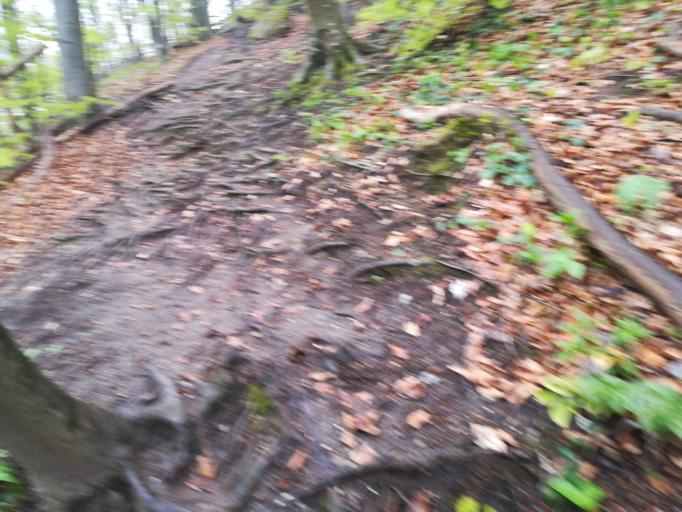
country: HR
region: Varazdinska
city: Ivanec
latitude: 46.1941
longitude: 16.1401
